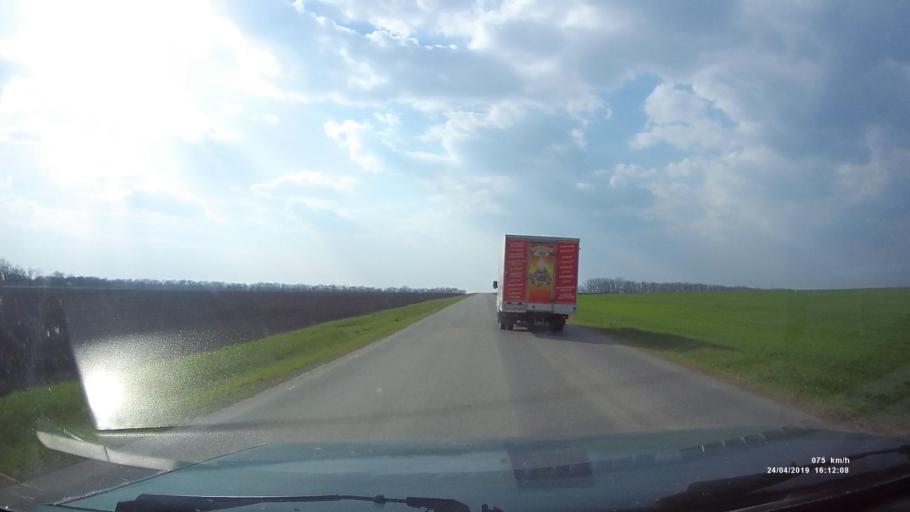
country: RU
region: Rostov
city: Sovetskoye
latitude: 46.7306
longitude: 42.2424
